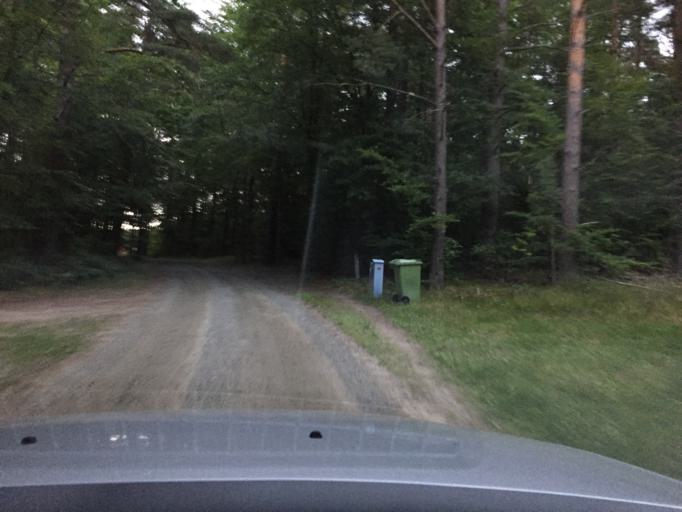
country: SE
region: Skane
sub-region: Kristianstads Kommun
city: Degeberga
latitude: 55.7319
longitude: 14.1241
